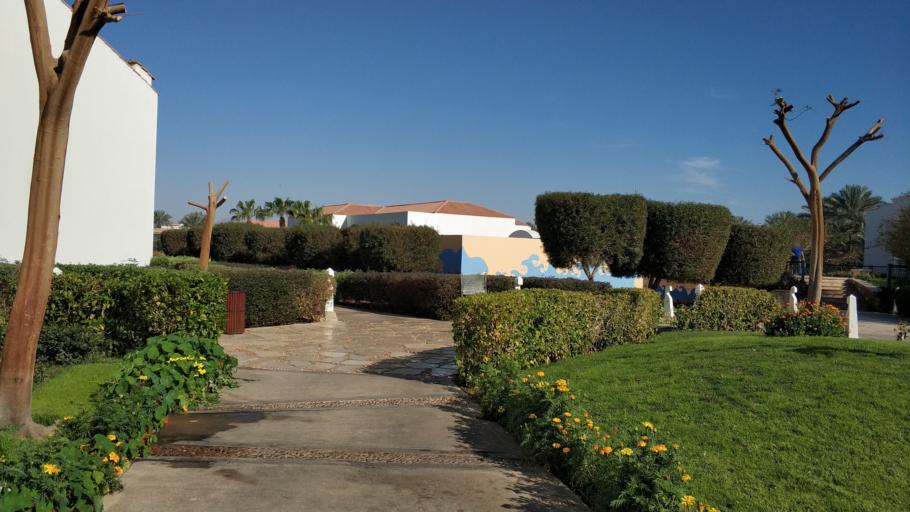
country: EG
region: South Sinai
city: Sharm el-Sheikh
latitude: 27.9193
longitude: 34.3613
